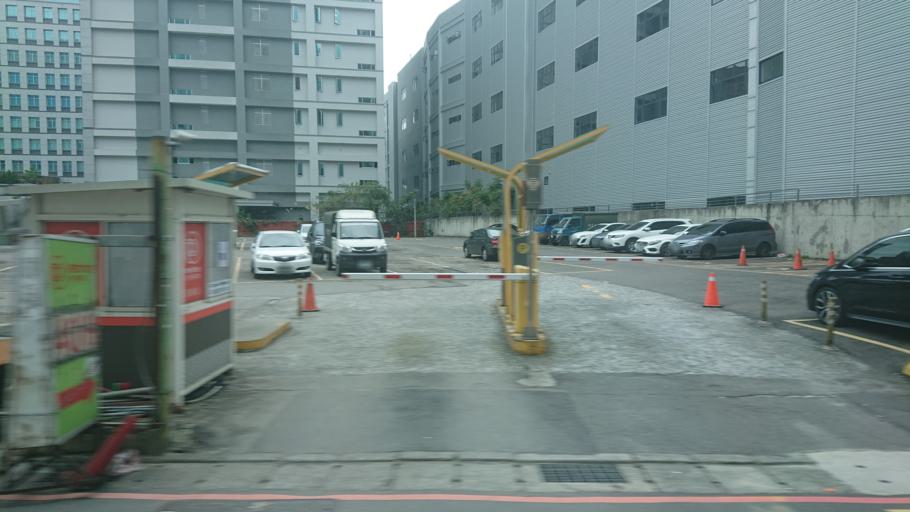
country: TW
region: Taipei
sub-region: Taipei
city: Banqiao
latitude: 24.9986
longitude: 121.4874
